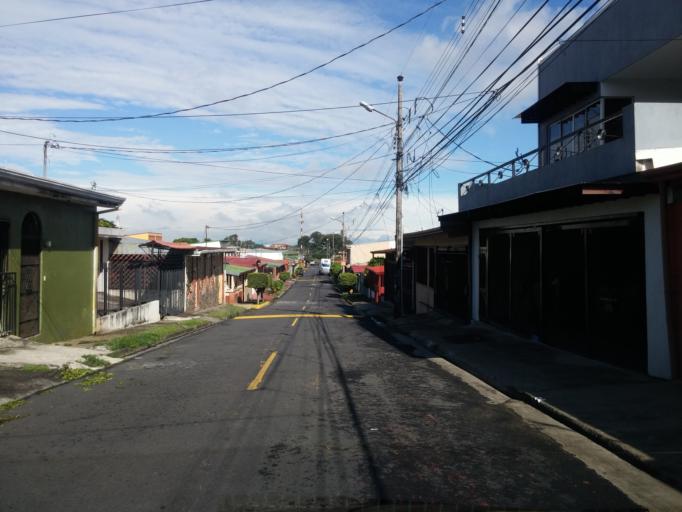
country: CR
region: Heredia
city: San Francisco
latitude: 9.9999
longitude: -84.1301
